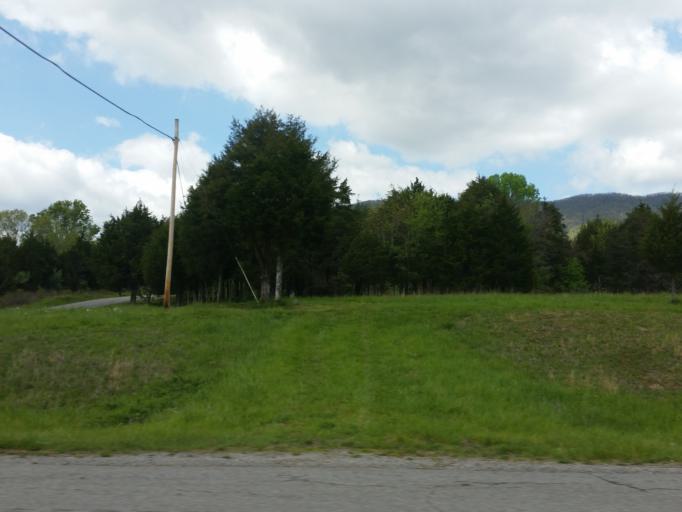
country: US
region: Tennessee
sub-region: Campbell County
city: Fincastle
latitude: 36.4464
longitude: -83.9435
